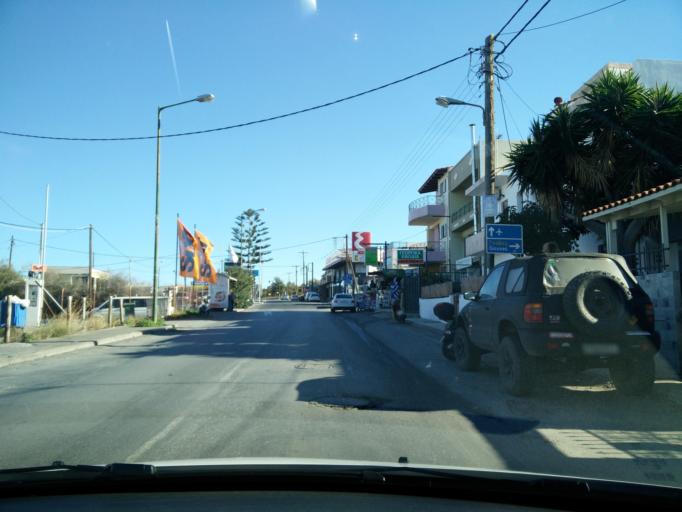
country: GR
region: Crete
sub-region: Nomos Irakleiou
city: Nea Alikarnassos
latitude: 35.3376
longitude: 25.1635
